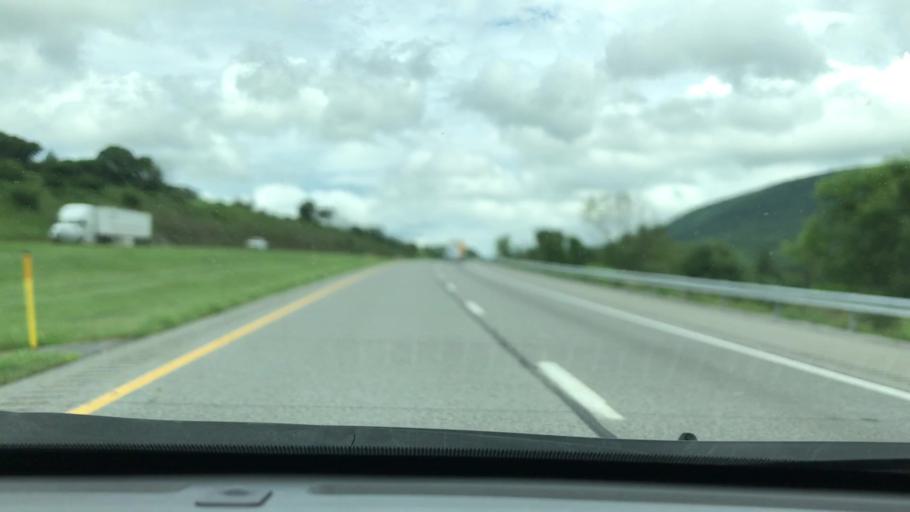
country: US
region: Pennsylvania
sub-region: Bedford County
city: Bedford
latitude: 40.1328
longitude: -78.5170
